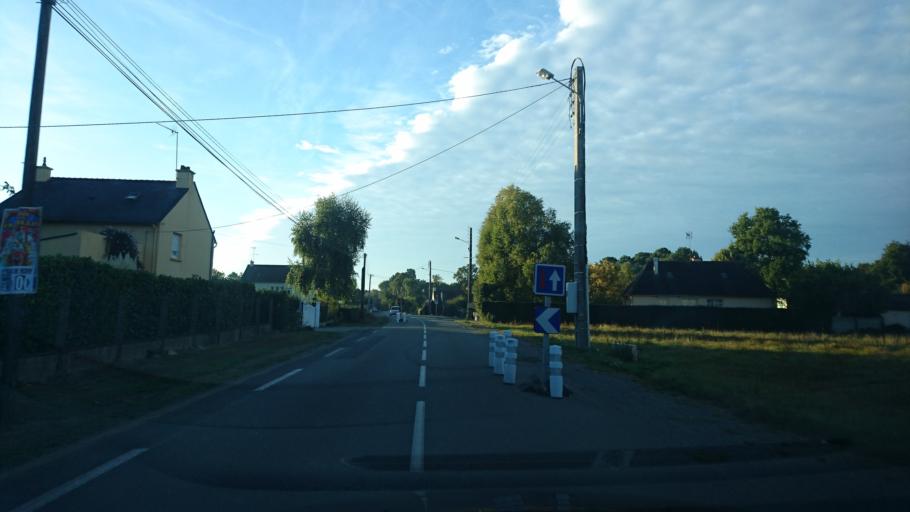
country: FR
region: Brittany
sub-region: Departement d'Ille-et-Vilaine
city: Bains-sur-Oust
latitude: 47.6974
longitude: -2.0598
